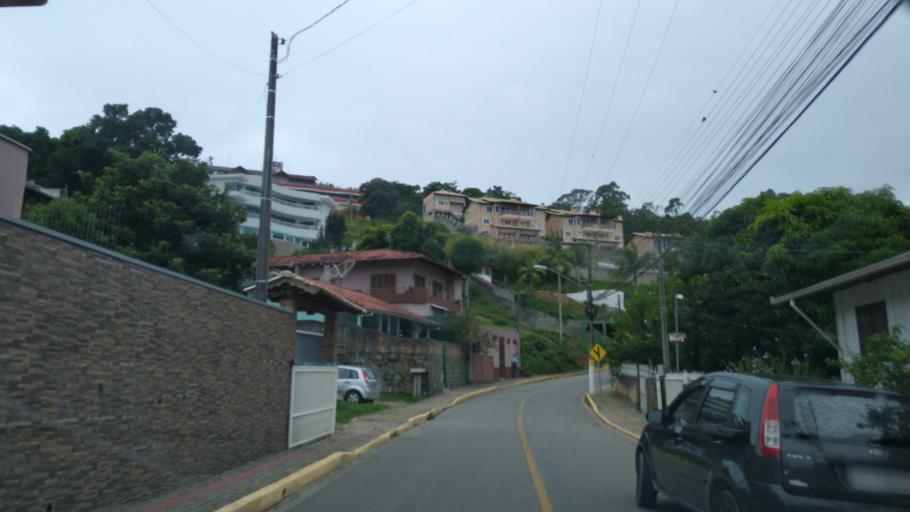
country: BR
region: Santa Catarina
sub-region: Itapema
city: Itapema
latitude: -27.0906
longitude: -48.6052
